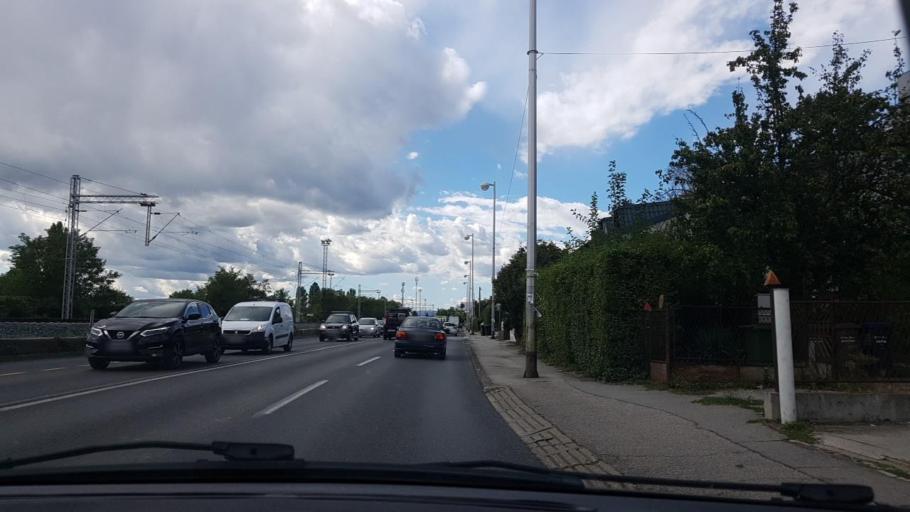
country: HR
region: Grad Zagreb
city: Jankomir
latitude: 45.8105
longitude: 15.9163
